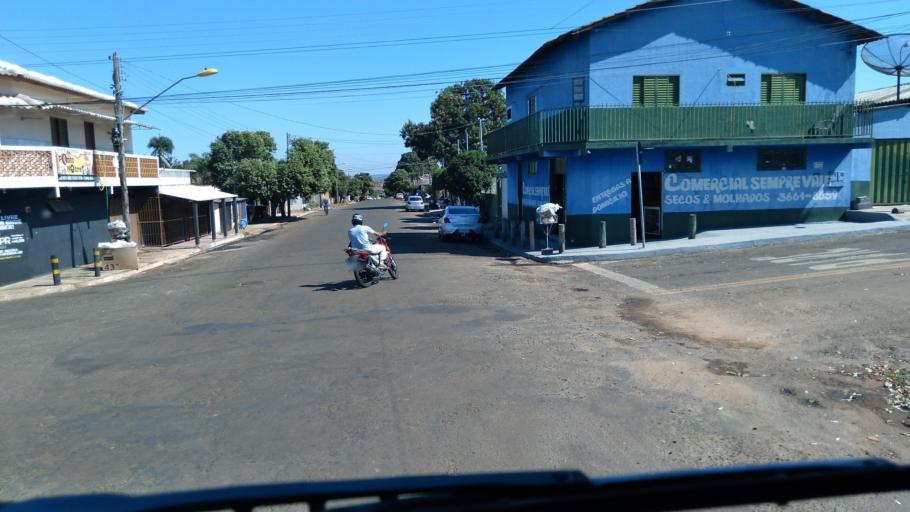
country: BR
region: Goias
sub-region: Mineiros
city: Mineiros
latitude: -17.5718
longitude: -52.5673
